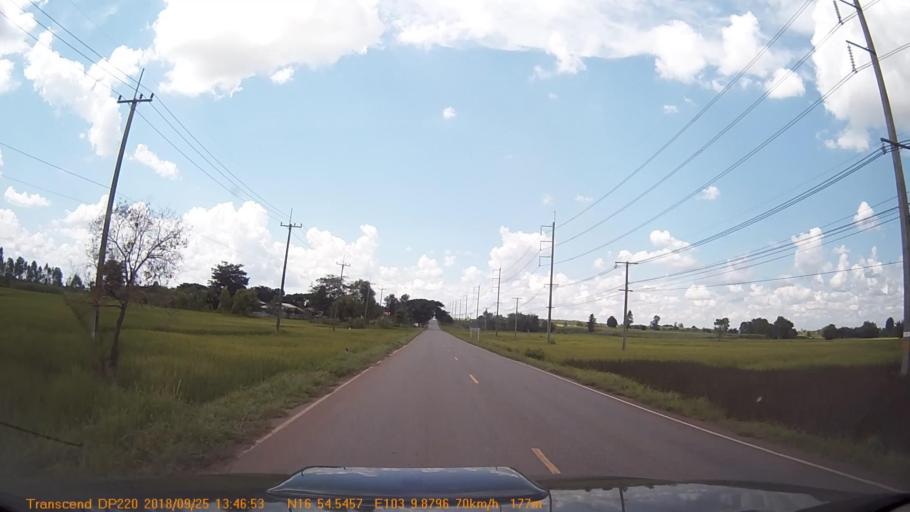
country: TH
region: Changwat Udon Thani
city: Si That
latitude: 16.9091
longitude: 103.1646
